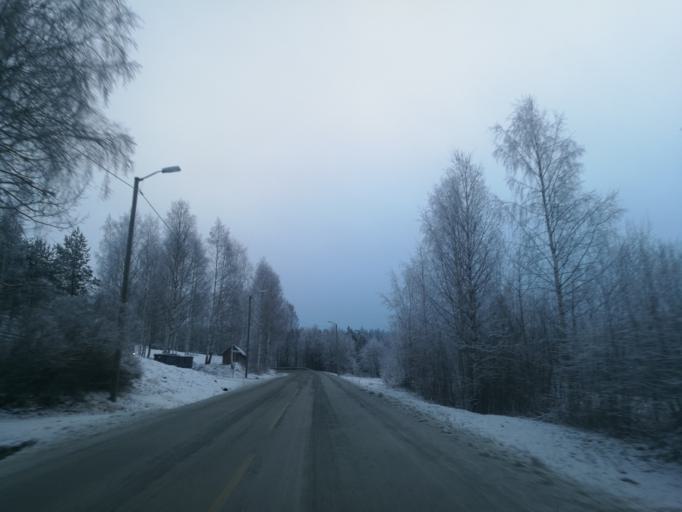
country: NO
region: Hedmark
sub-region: Kongsvinger
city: Kongsvinger
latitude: 60.2775
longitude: 12.1453
